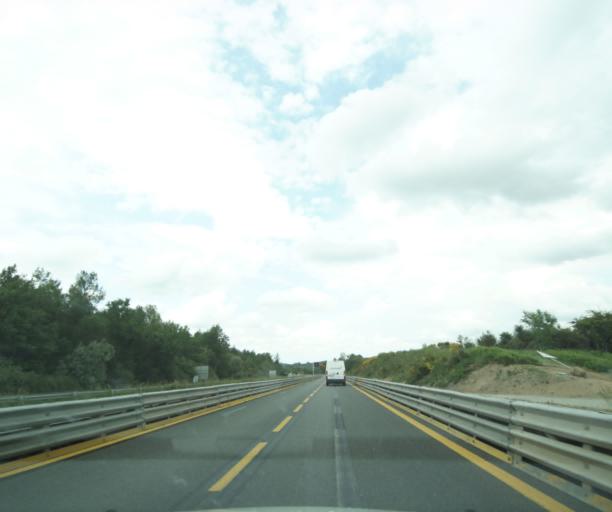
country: FR
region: Auvergne
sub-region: Departement de l'Allier
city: Ebreuil
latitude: 46.0657
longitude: 3.1176
